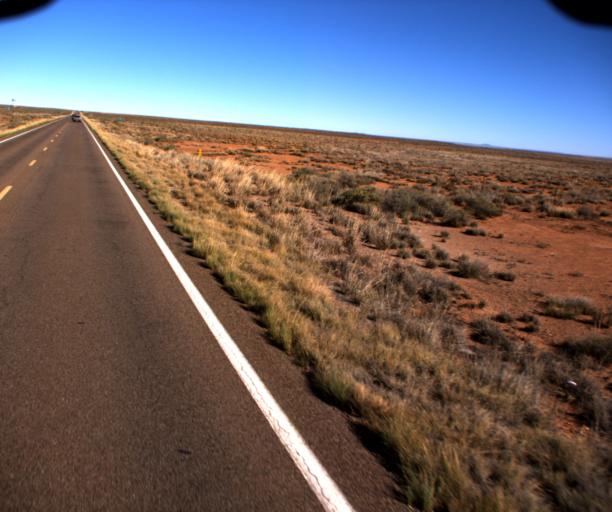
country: US
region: Arizona
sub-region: Navajo County
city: Holbrook
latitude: 34.7249
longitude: -110.1152
